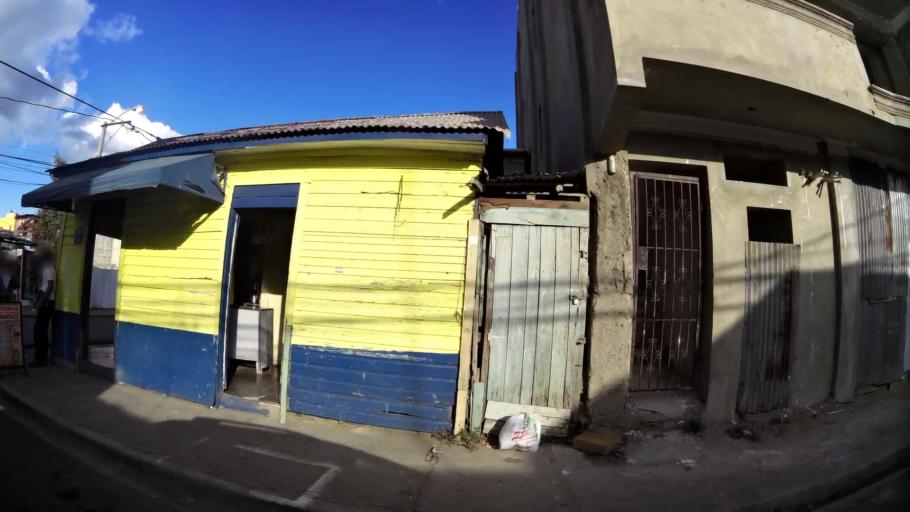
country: DO
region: Santiago
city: Santiago de los Caballeros
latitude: 19.4590
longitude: -70.7077
